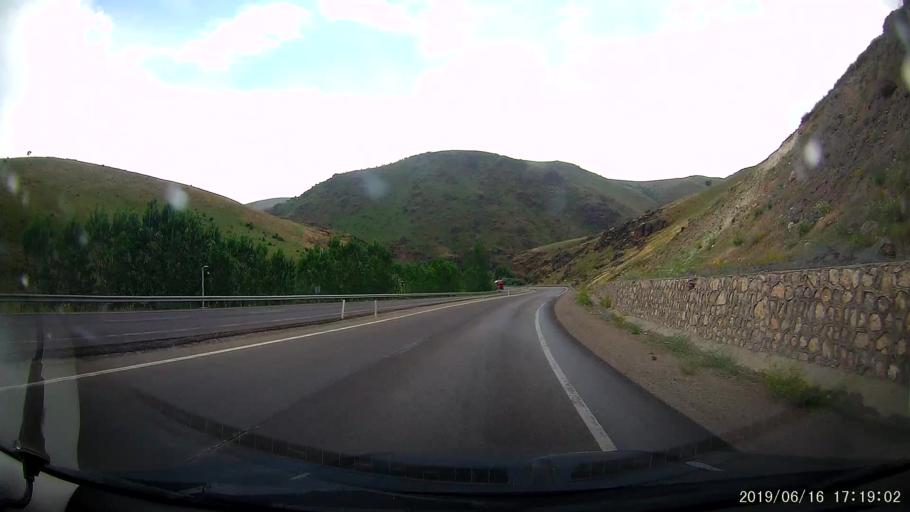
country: TR
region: Erzincan
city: Tercan
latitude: 39.8055
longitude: 40.5316
